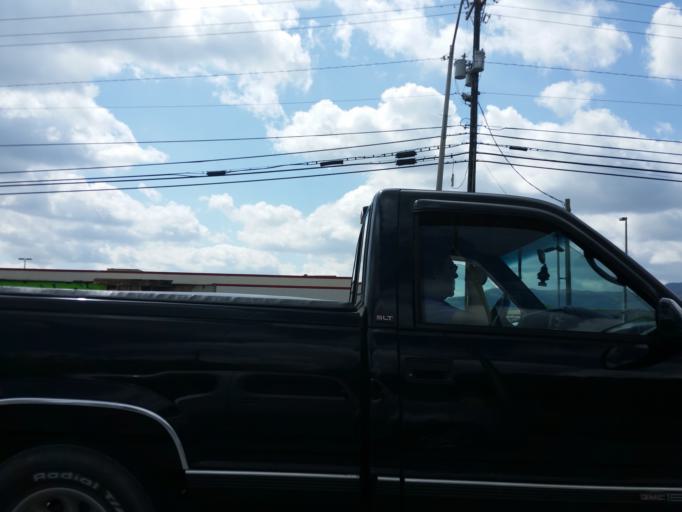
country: US
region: Kentucky
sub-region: Bell County
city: Middlesboro
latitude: 36.6186
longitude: -83.7036
